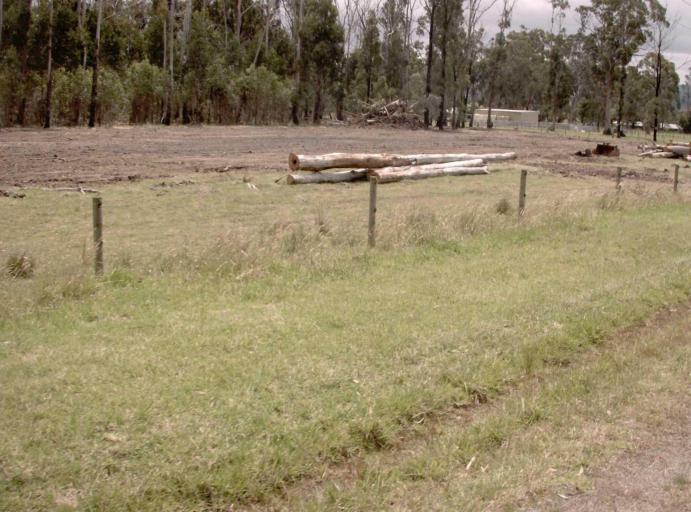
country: AU
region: Victoria
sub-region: Latrobe
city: Traralgon
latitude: -38.5323
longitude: 146.6584
